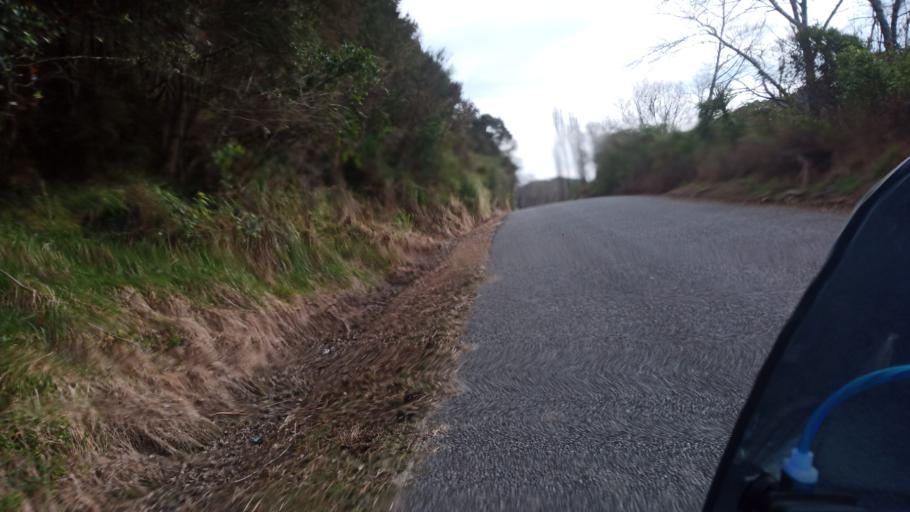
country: NZ
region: Hawke's Bay
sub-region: Wairoa District
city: Wairoa
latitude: -38.8222
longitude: 177.4959
